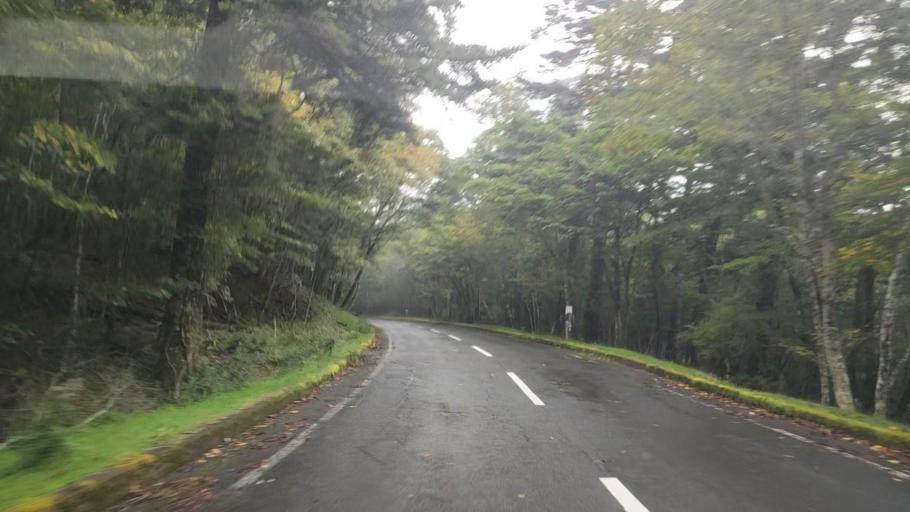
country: JP
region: Shizuoka
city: Fujinomiya
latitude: 35.3165
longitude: 138.7312
